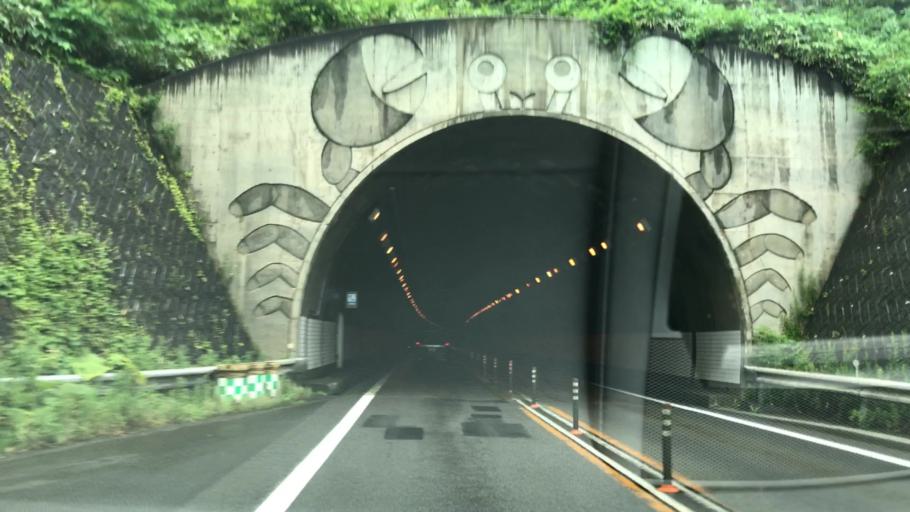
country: JP
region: Hokkaido
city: Muroran
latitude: 42.3849
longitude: 141.0180
